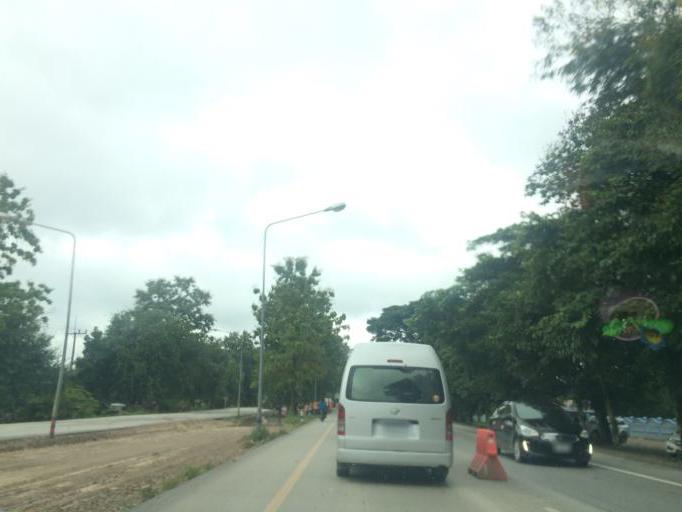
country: TH
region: Chiang Rai
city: Chiang Rai
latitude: 19.8444
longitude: 99.8012
